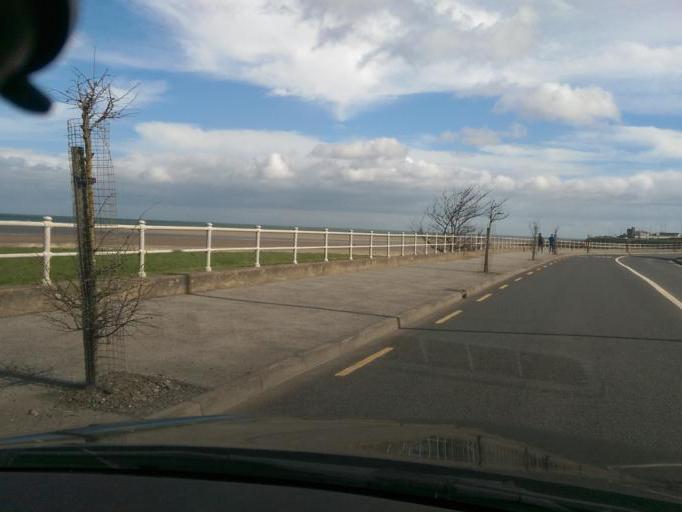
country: IE
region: Leinster
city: Malahide
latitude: 53.4483
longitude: -6.1363
